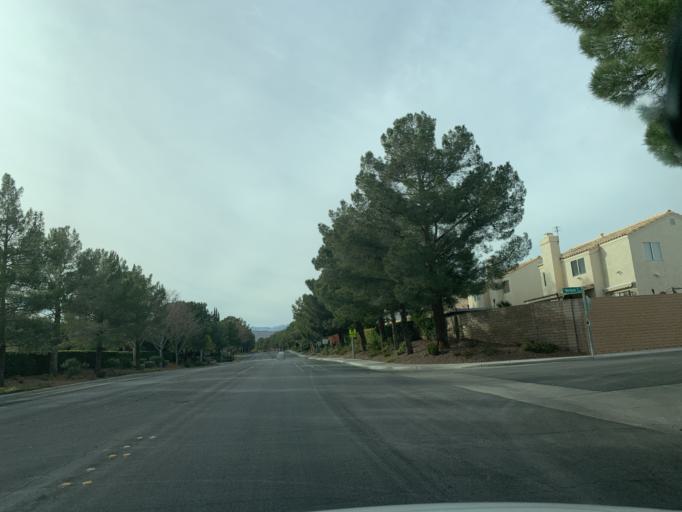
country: US
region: Nevada
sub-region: Clark County
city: Summerlin South
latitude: 36.1407
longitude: -115.3045
